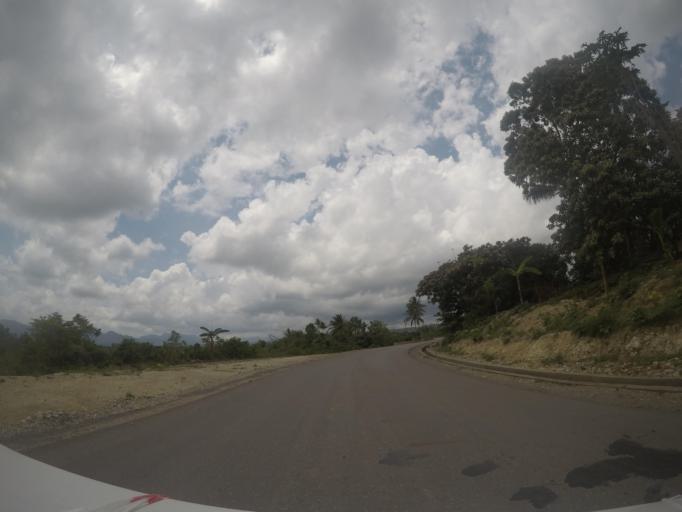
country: TL
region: Baucau
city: Venilale
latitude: -8.5584
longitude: 126.4029
